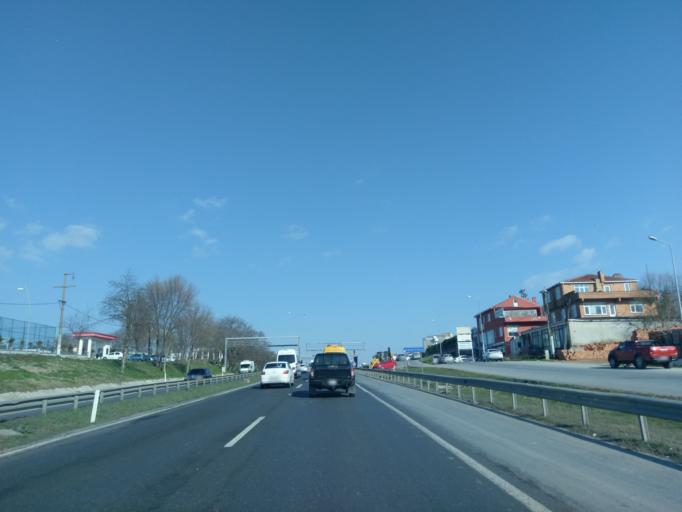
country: TR
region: Istanbul
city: Chekmejeh
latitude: 41.0097
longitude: 28.5262
